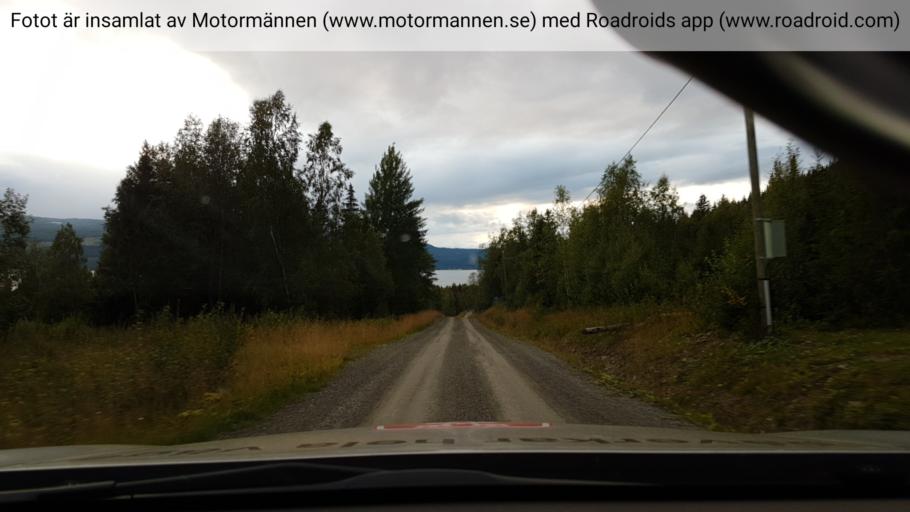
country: SE
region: Vaesterbotten
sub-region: Vilhelmina Kommun
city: Sjoberg
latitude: 65.6138
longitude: 15.2586
